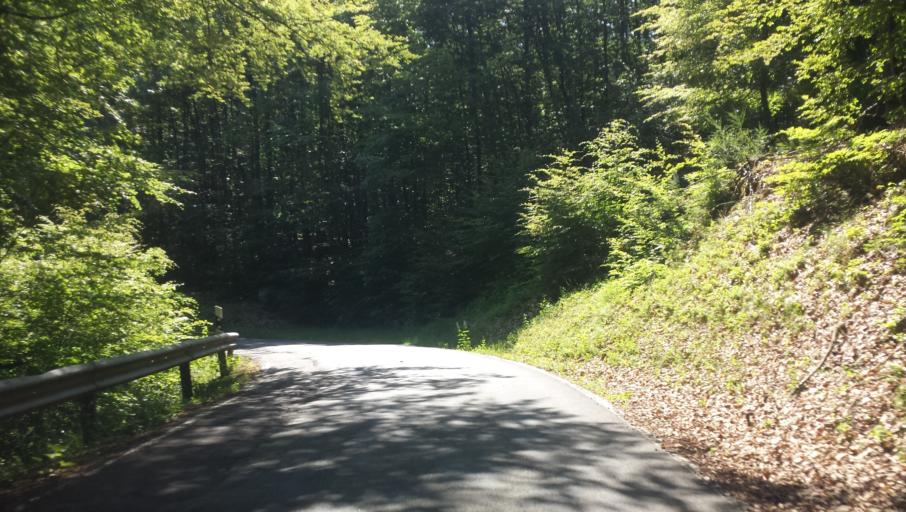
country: DE
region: Rheinland-Pfalz
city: Waldleiningen
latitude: 49.3801
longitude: 7.8935
